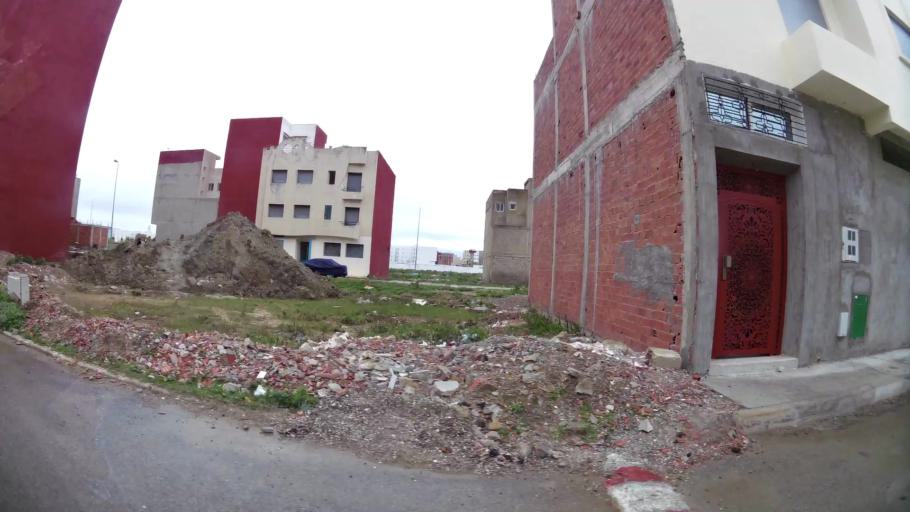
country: MA
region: Tanger-Tetouan
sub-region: Tetouan
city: Martil
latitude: 35.6139
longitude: -5.2982
